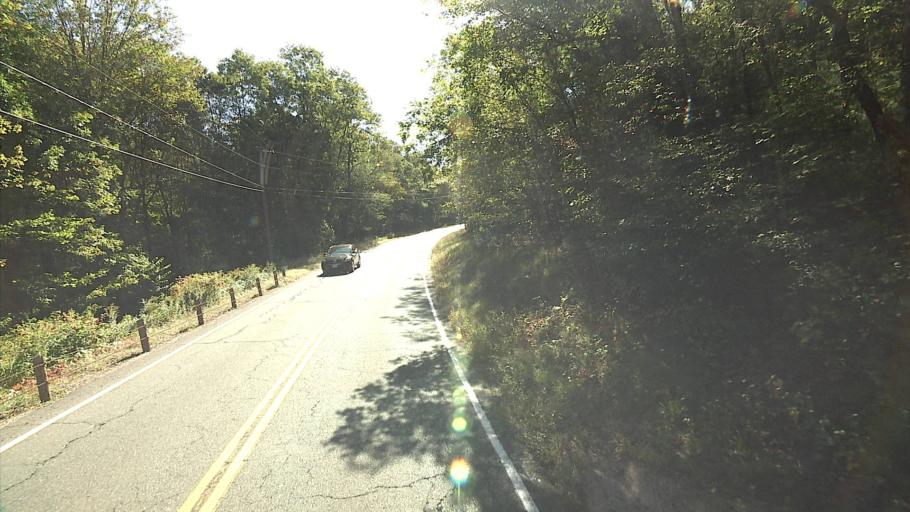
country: US
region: Connecticut
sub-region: Hartford County
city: Bristol
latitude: 41.7408
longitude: -72.9652
